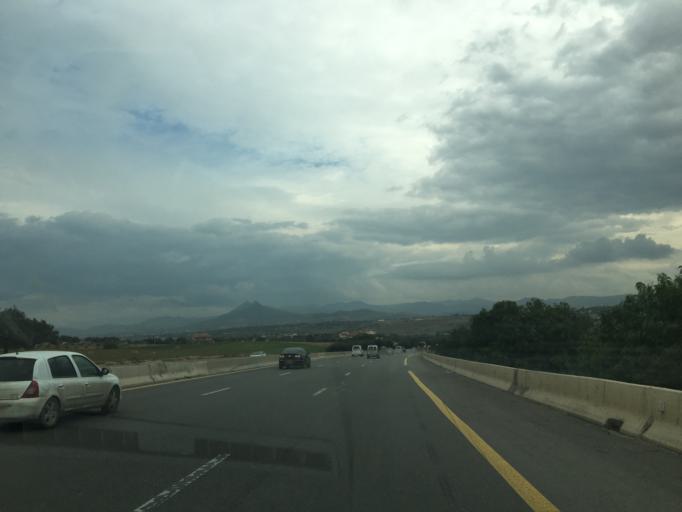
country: DZ
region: Bouira
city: Bouira
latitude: 36.3201
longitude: 4.0002
